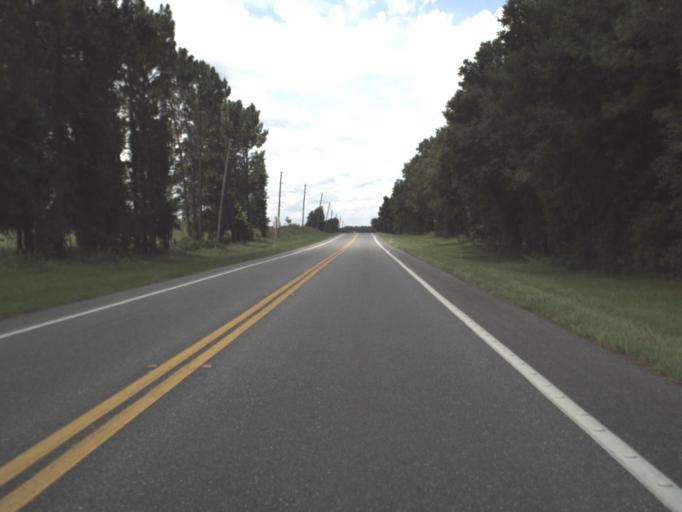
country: US
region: Florida
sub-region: Levy County
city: Williston Highlands
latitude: 29.3611
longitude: -82.5034
